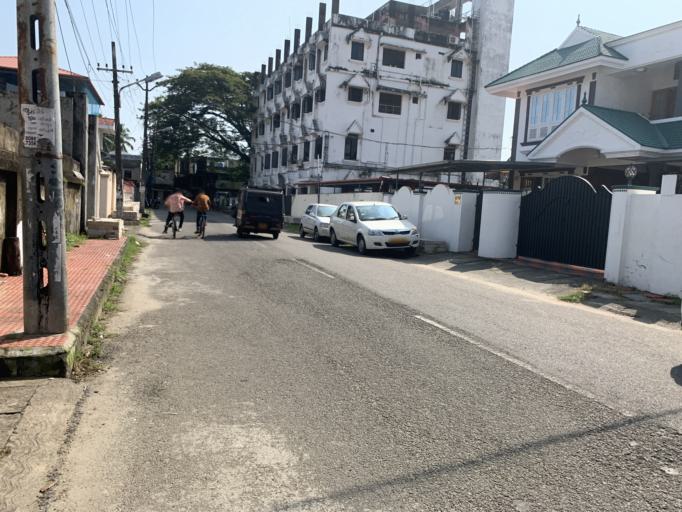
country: IN
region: Kerala
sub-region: Ernakulam
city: Cochin
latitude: 9.9607
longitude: 76.2567
